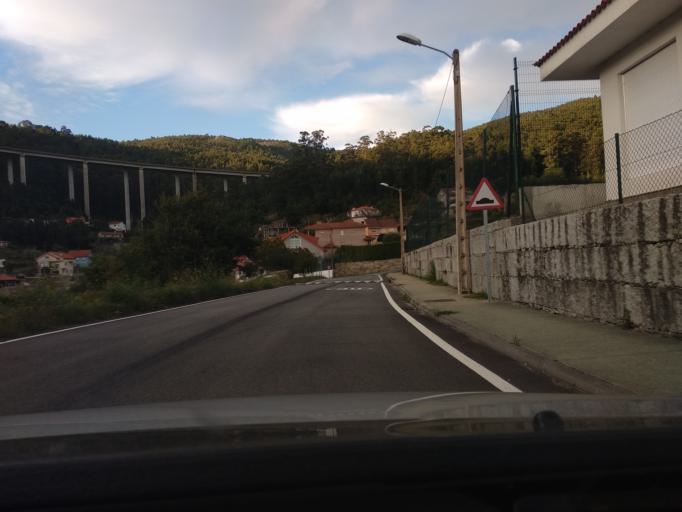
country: ES
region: Galicia
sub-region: Provincia de Pontevedra
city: Moana
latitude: 42.2940
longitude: -8.6798
